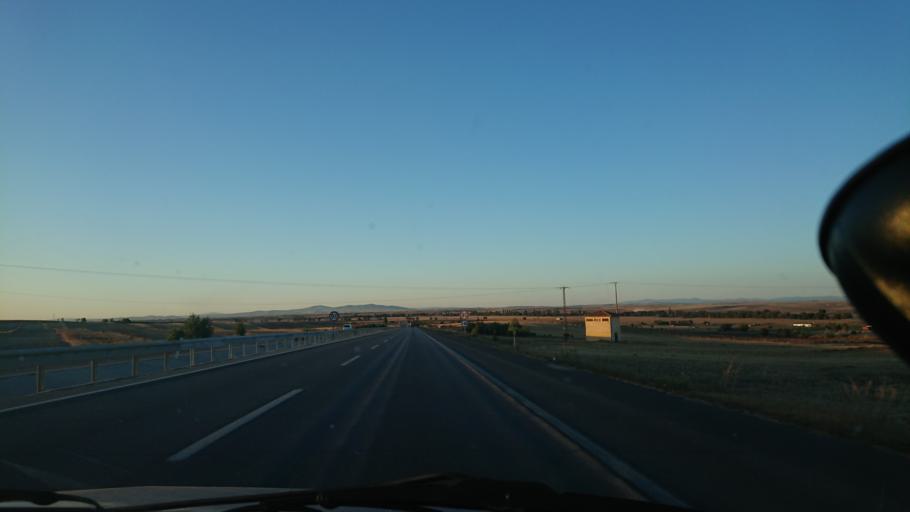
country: TR
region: Eskisehir
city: Mahmudiye
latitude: 39.5102
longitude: 30.9647
